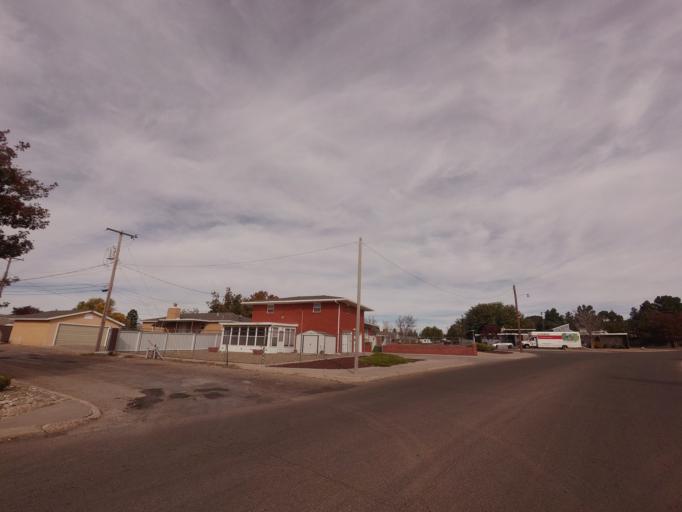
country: US
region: New Mexico
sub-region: Curry County
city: Clovis
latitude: 34.4199
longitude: -103.2097
